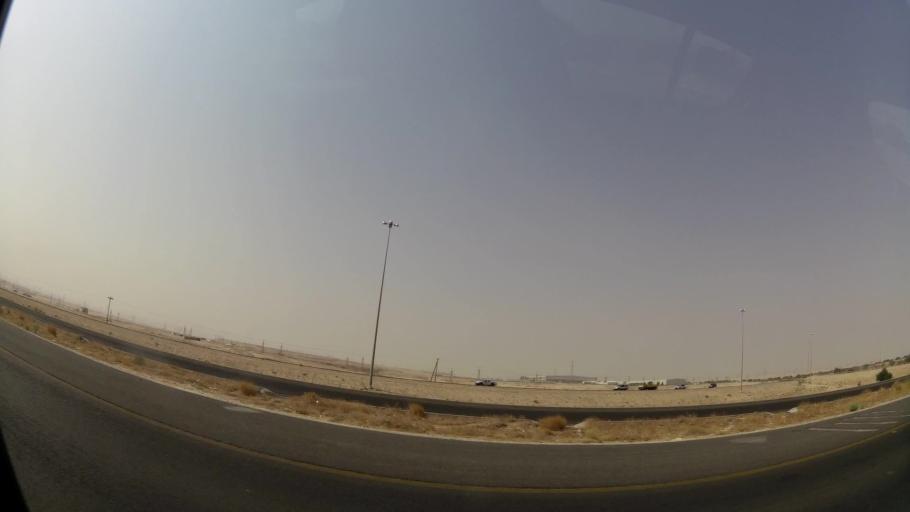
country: KW
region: Muhafazat al Jahra'
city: Al Jahra'
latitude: 29.3346
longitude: 47.6313
